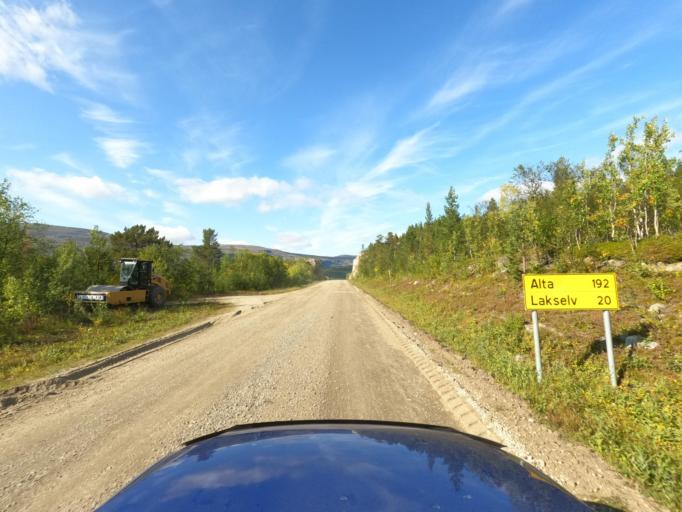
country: NO
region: Finnmark Fylke
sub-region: Porsanger
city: Lakselv
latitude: 69.8895
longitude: 25.0054
